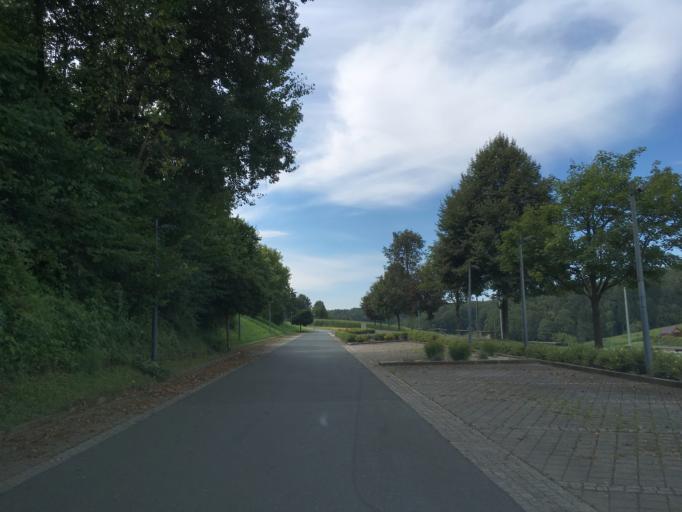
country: AT
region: Styria
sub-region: Politischer Bezirk Leibnitz
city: Pistorf
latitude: 46.7920
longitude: 15.3767
